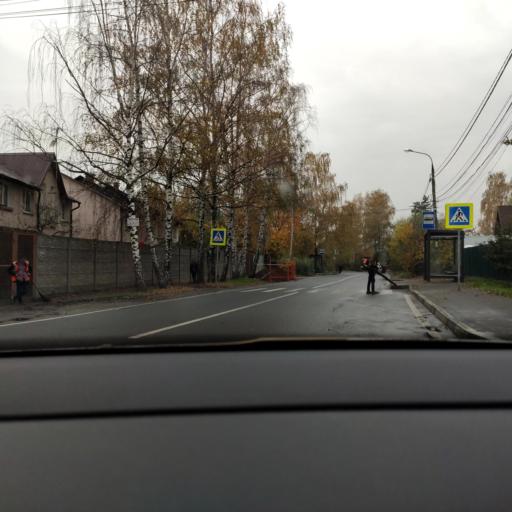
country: RU
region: Moskovskaya
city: Druzhba
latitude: 55.8855
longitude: 37.7529
